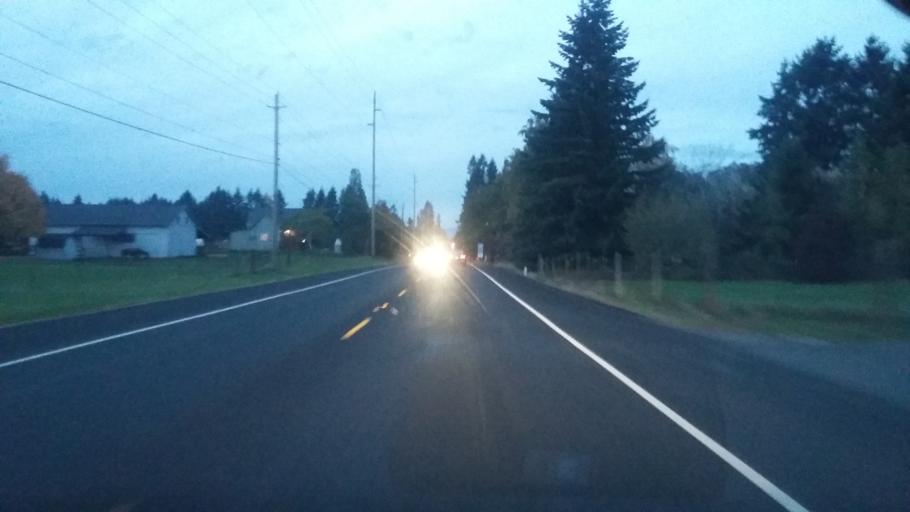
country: US
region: Washington
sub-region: Clark County
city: Barberton
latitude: 45.7152
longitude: -122.5994
